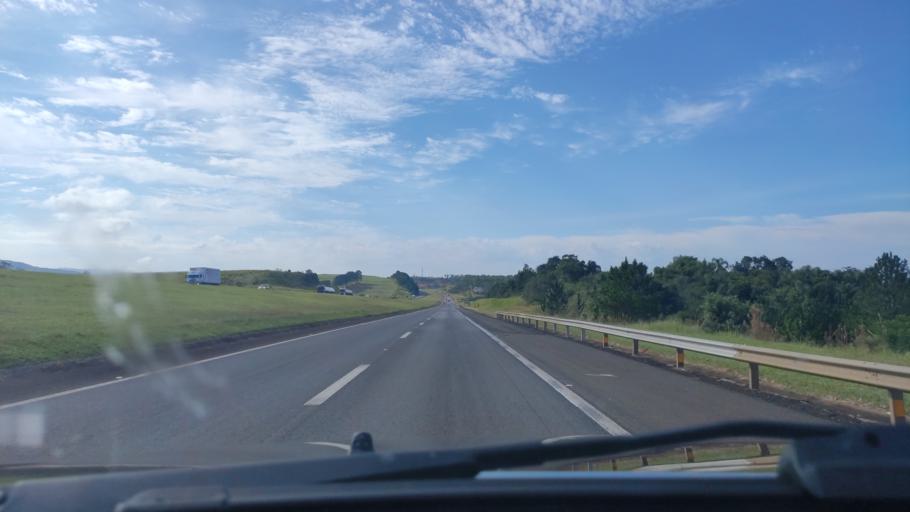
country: BR
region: Sao Paulo
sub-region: Itatinga
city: Itatinga
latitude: -23.1274
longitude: -48.4746
